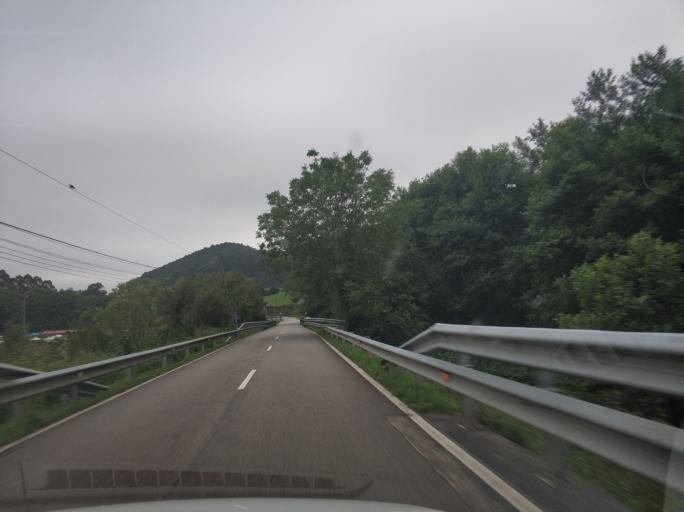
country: ES
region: Asturias
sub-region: Province of Asturias
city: Cudillero
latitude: 43.5530
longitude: -6.1938
